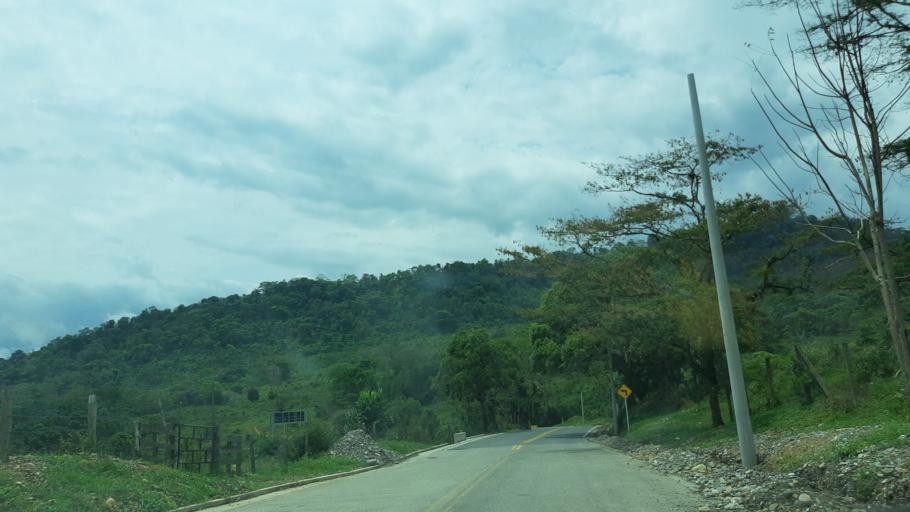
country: CO
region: Casanare
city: Sabanalarga
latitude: 4.8248
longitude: -73.0856
